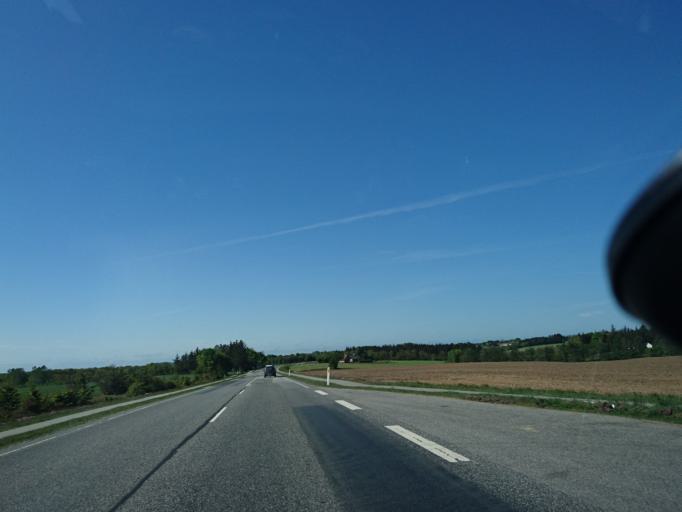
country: DK
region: North Denmark
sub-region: Hjorring Kommune
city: Sindal
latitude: 57.4600
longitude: 10.1468
